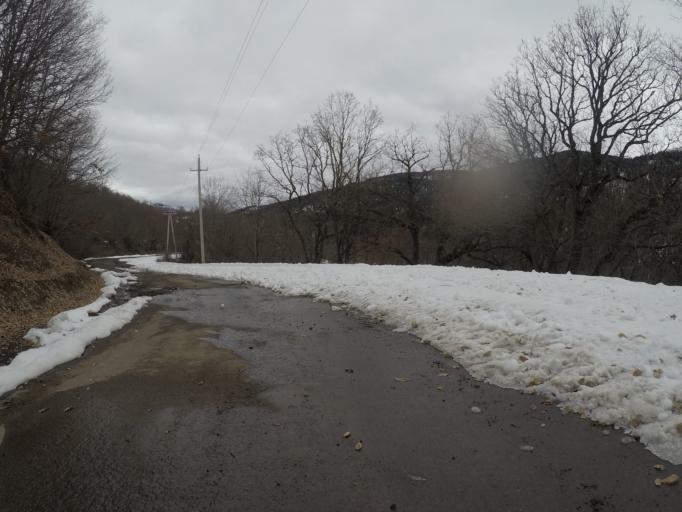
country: GE
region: Samtskhe-Javakheti
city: Adigeni
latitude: 41.6668
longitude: 42.6244
